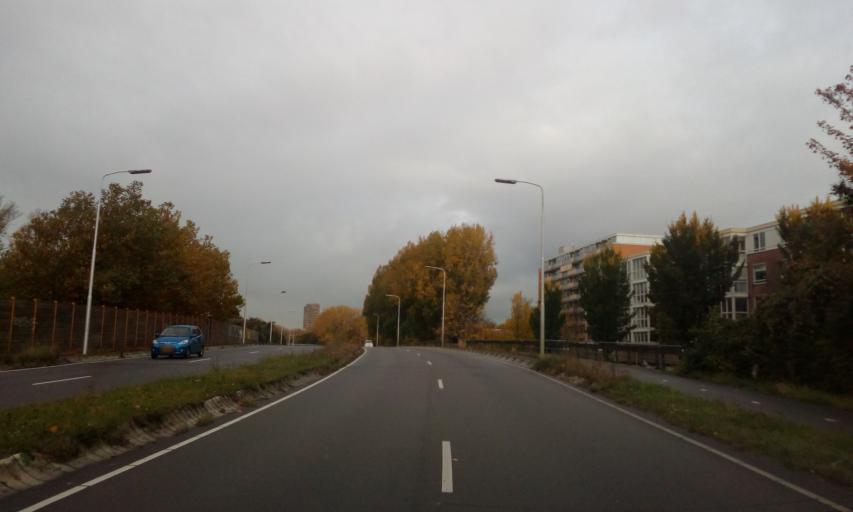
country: NL
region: South Holland
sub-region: Gemeente Delft
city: Delft
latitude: 52.0043
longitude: 4.3474
